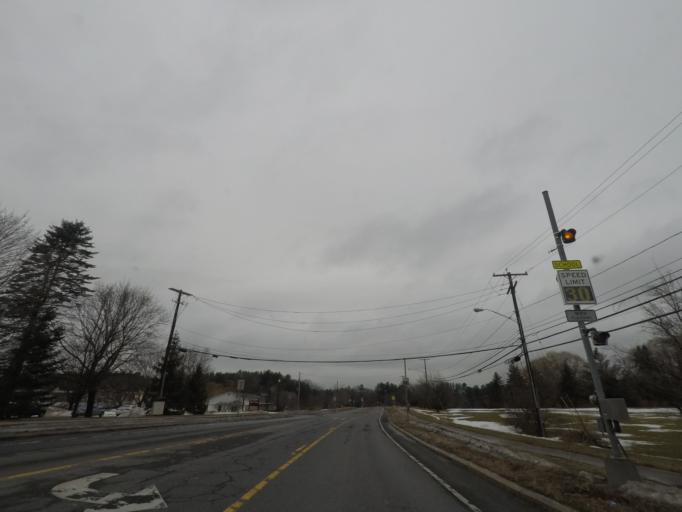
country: US
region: New York
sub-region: Albany County
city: Westmere
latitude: 42.6923
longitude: -73.8940
